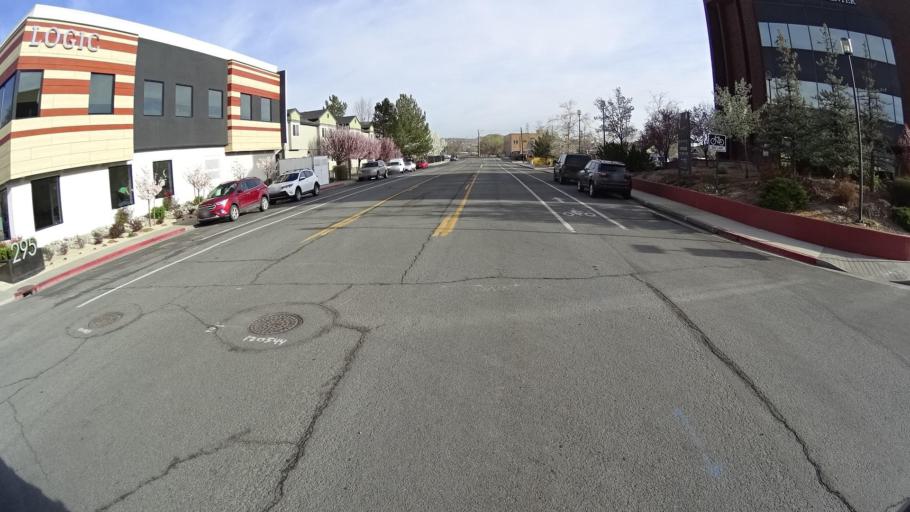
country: US
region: Nevada
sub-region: Washoe County
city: Reno
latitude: 39.5237
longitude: -119.8064
